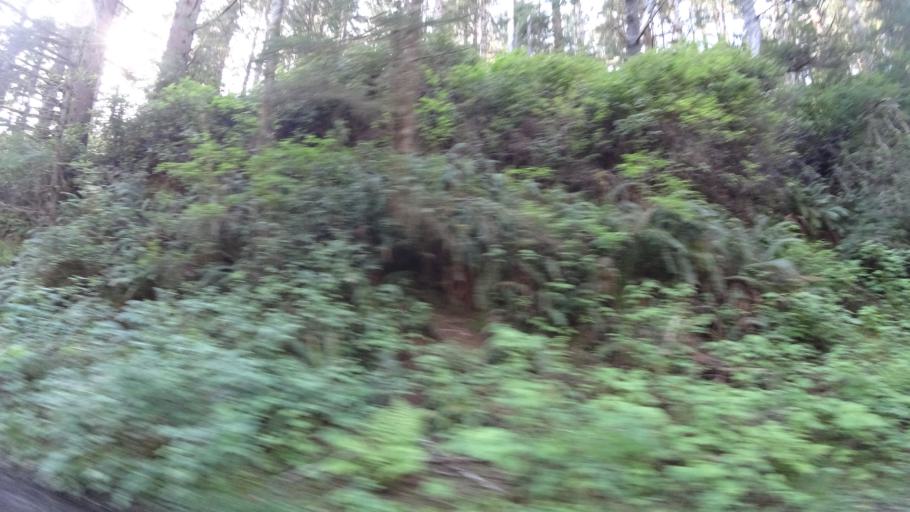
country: US
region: Oregon
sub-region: Douglas County
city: Reedsport
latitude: 43.7452
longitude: -124.1701
